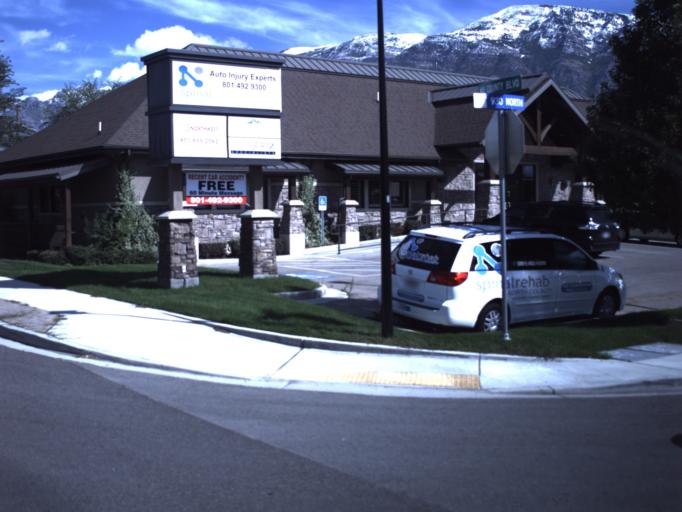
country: US
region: Utah
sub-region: Utah County
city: American Fork
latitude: 40.3738
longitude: -111.7691
